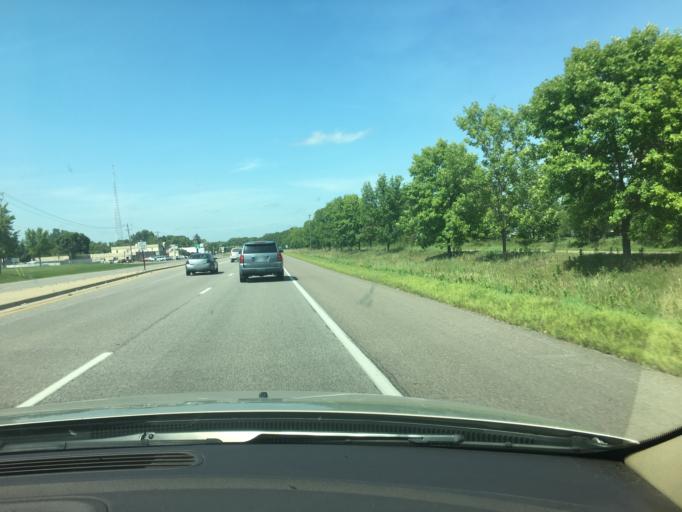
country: US
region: Minnesota
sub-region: Stearns County
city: Saint Cloud
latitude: 45.5316
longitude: -94.1639
